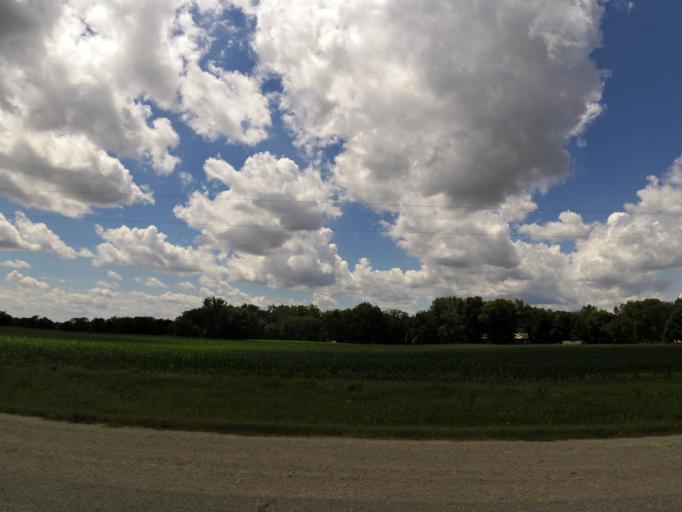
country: US
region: Iowa
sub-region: Fayette County
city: Oelwein
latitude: 42.6401
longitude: -91.9086
